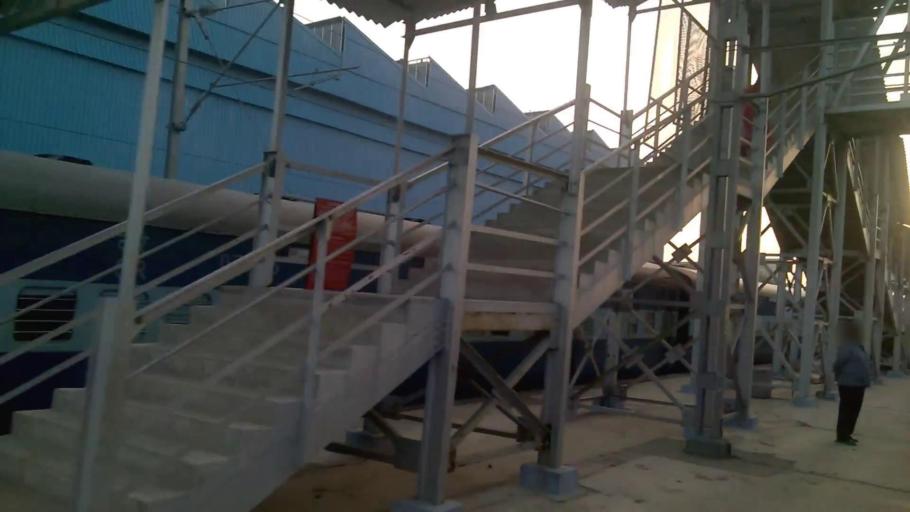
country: IN
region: Tamil Nadu
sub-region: Thoothukkudi
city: Korampallam
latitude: 8.8064
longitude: 78.1542
